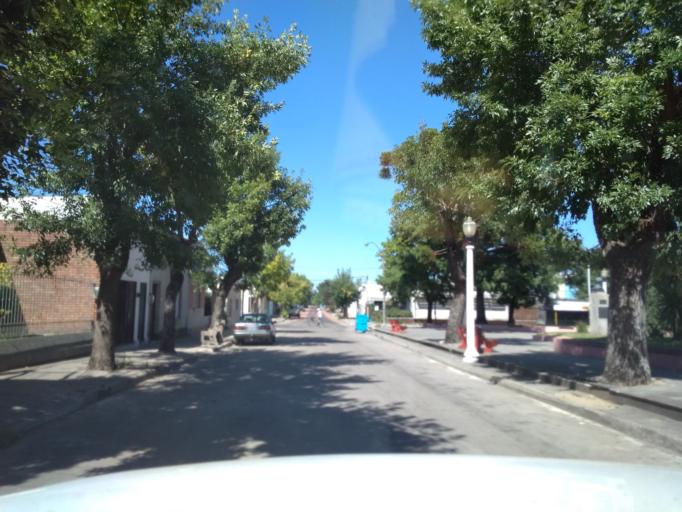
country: UY
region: Florida
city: Florida
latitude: -34.1001
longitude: -56.2190
